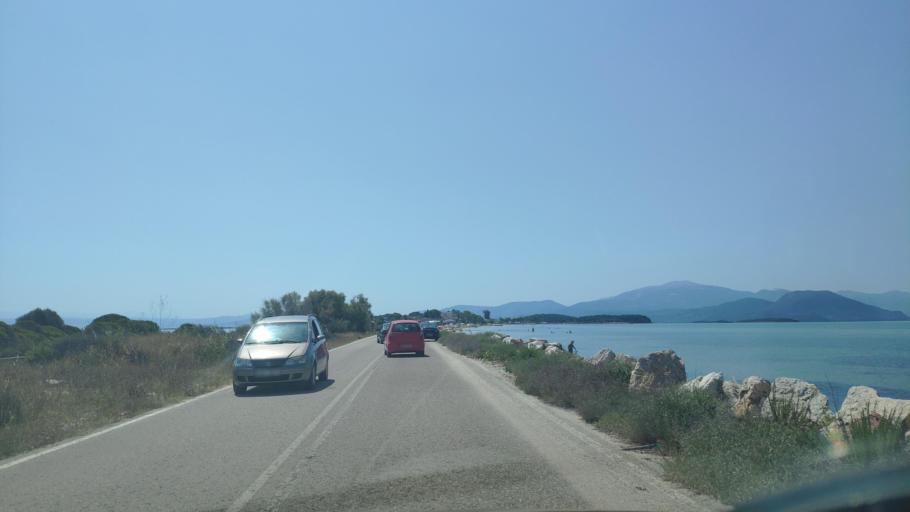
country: GR
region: Epirus
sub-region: Nomos Artas
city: Aneza
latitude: 39.0247
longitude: 20.9079
